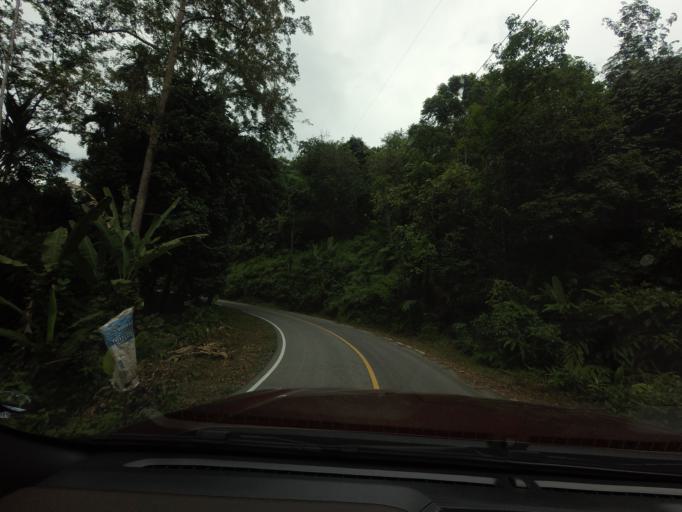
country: TH
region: Narathiwat
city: Sukhirin
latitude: 5.9786
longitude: 101.6814
